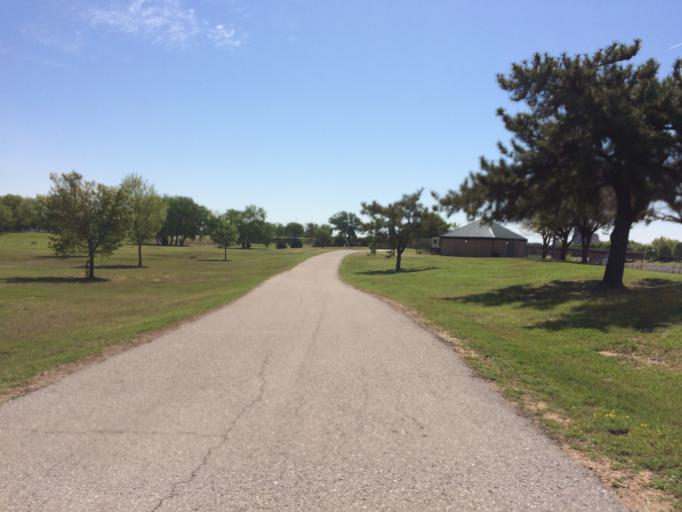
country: US
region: Oklahoma
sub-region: Oklahoma County
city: Oklahoma City
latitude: 35.4505
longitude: -97.5250
